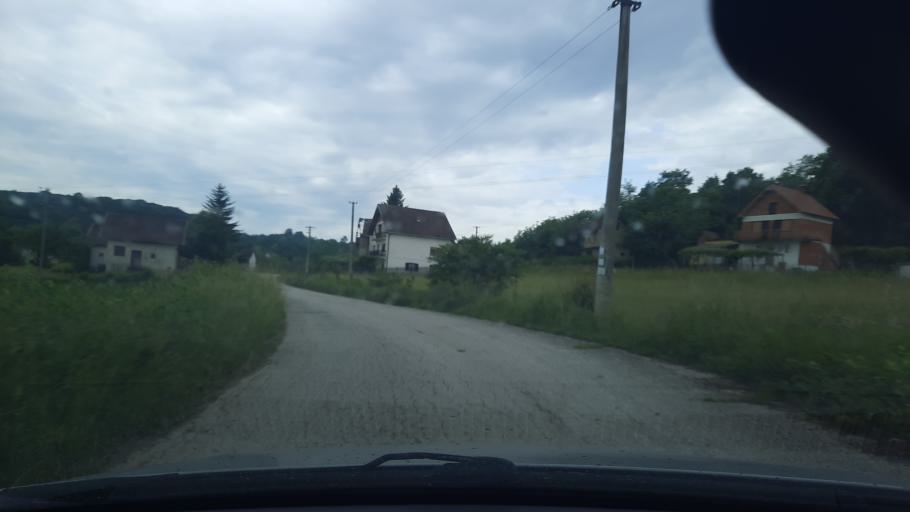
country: RS
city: Jarebice
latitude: 44.4835
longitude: 19.4824
